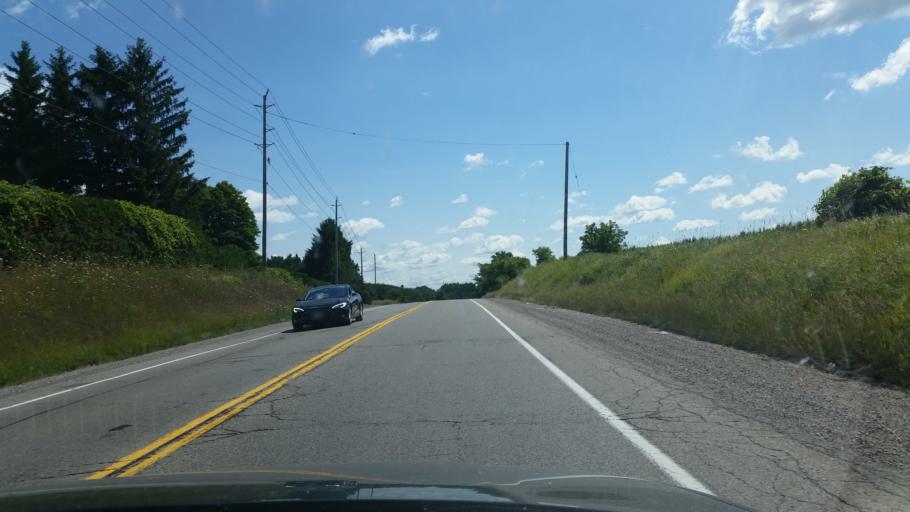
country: CA
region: Ontario
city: Vaughan
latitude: 43.9107
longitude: -79.6121
